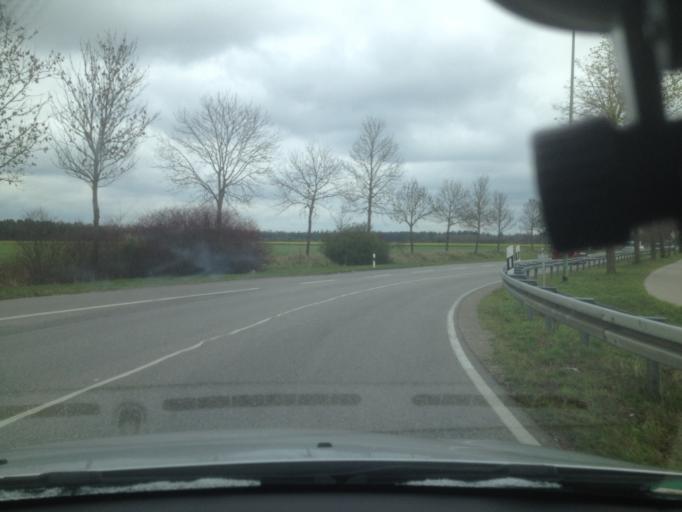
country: DE
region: Bavaria
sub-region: Swabia
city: Konigsbrunn
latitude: 48.2650
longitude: 10.9040
